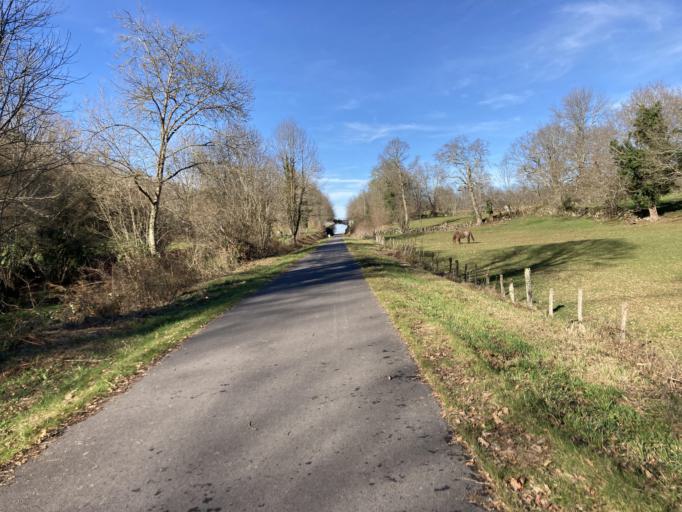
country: FR
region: Aquitaine
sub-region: Departement des Pyrenees-Atlantiques
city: Arudy
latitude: 43.1244
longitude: -0.4407
